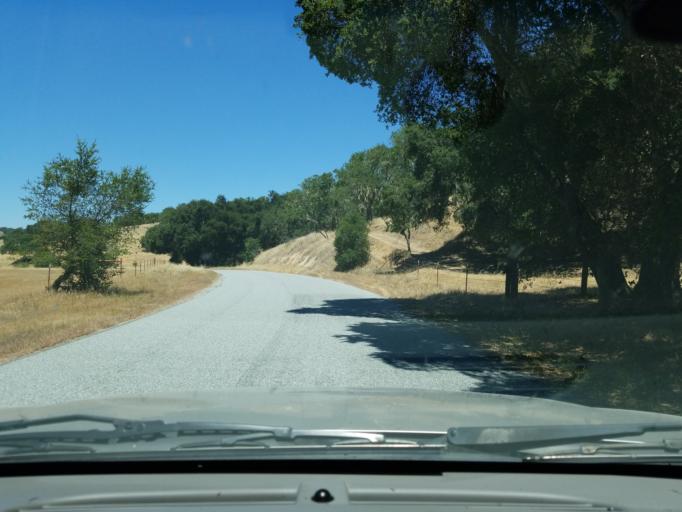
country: US
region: California
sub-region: Monterey County
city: Gonzales
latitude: 36.3931
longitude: -121.5680
